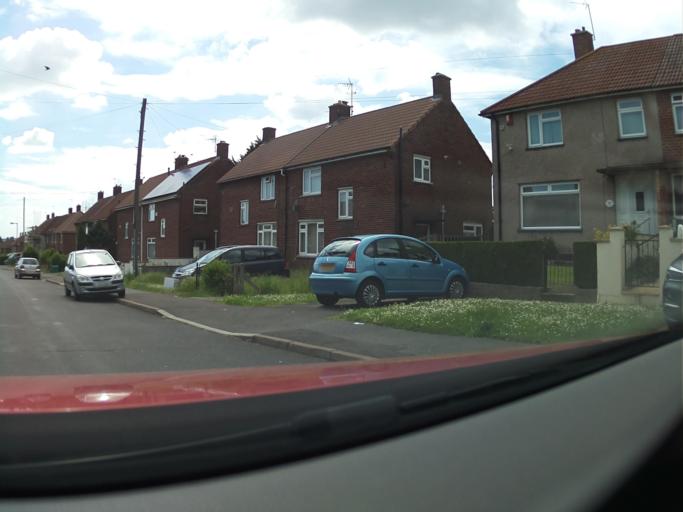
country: GB
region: England
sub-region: Bristol
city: Bristol
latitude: 51.5045
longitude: -2.6079
